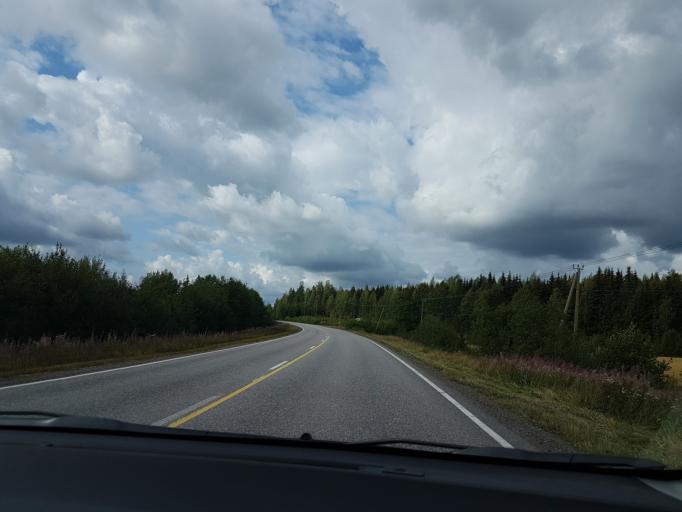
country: FI
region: Uusimaa
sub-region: Helsinki
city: Pornainen
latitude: 60.4770
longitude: 25.3219
